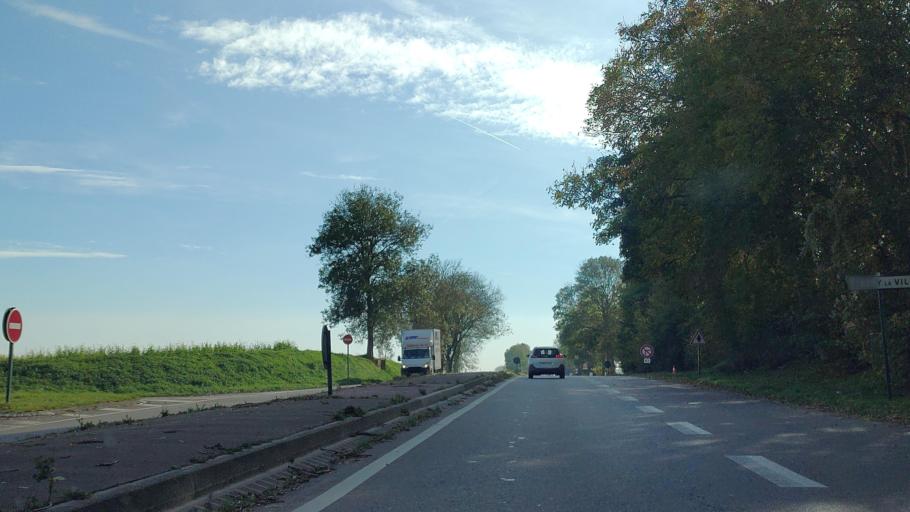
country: FR
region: Ile-de-France
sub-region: Departement du Val-d'Oise
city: Survilliers
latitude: 49.0790
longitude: 2.5292
